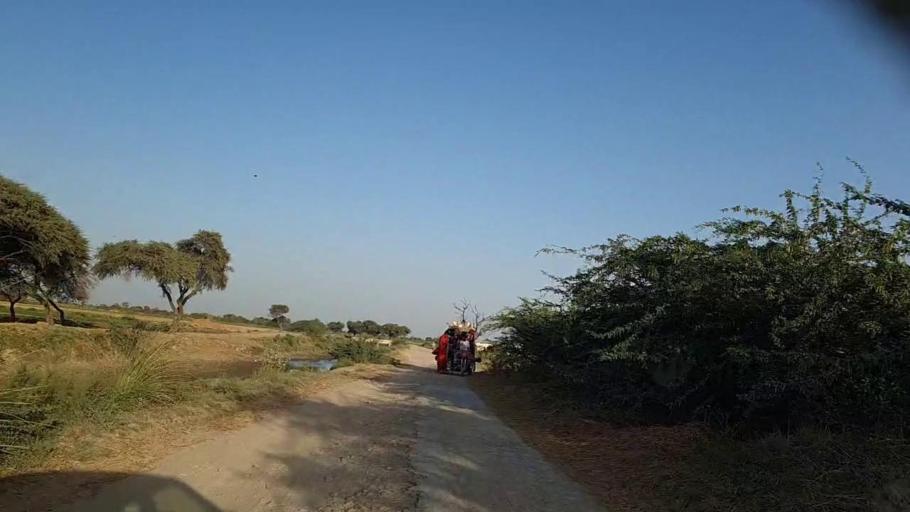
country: PK
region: Sindh
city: Jati
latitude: 24.4145
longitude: 68.3135
